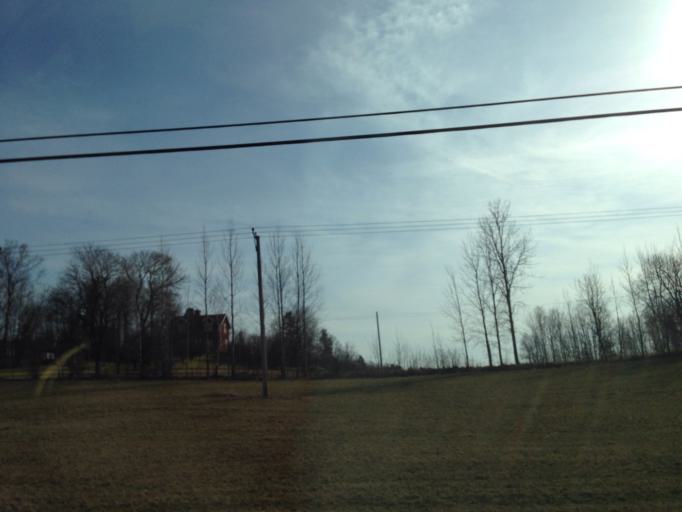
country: SE
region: Soedermanland
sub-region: Strangnas Kommun
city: Akers Styckebruk
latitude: 59.0780
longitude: 16.9810
